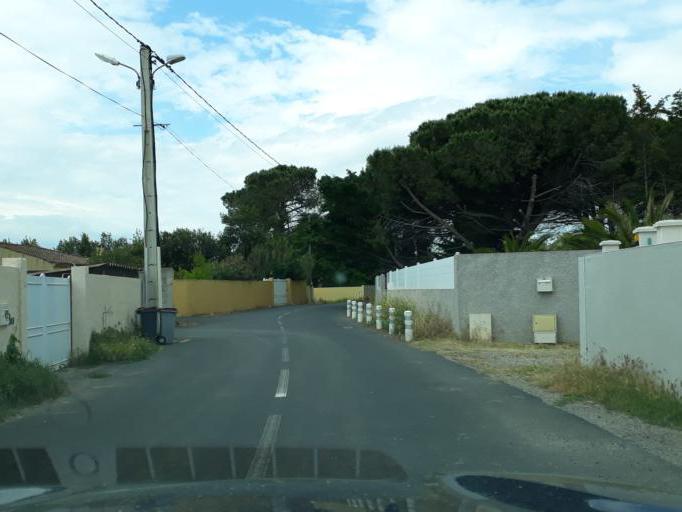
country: FR
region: Languedoc-Roussillon
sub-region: Departement de l'Herault
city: Agde
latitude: 43.2876
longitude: 3.4662
